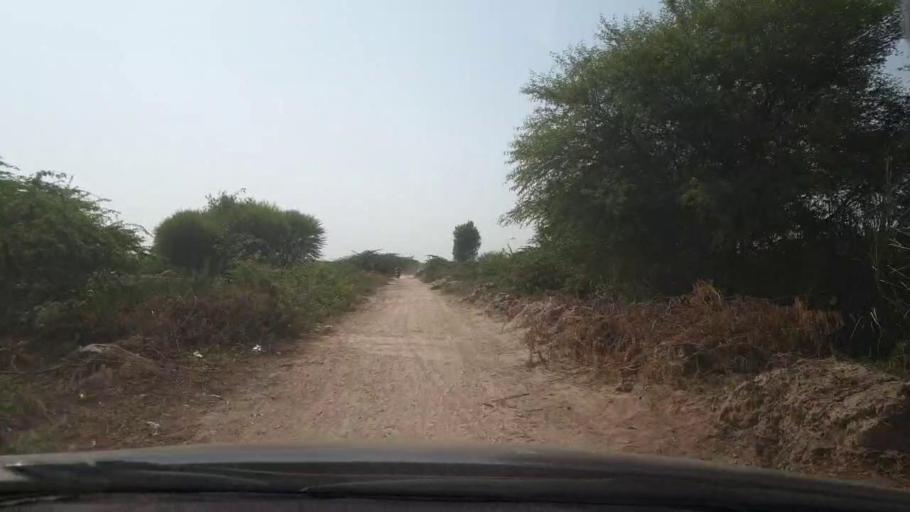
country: PK
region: Sindh
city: Naukot
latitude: 24.7957
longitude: 69.2398
